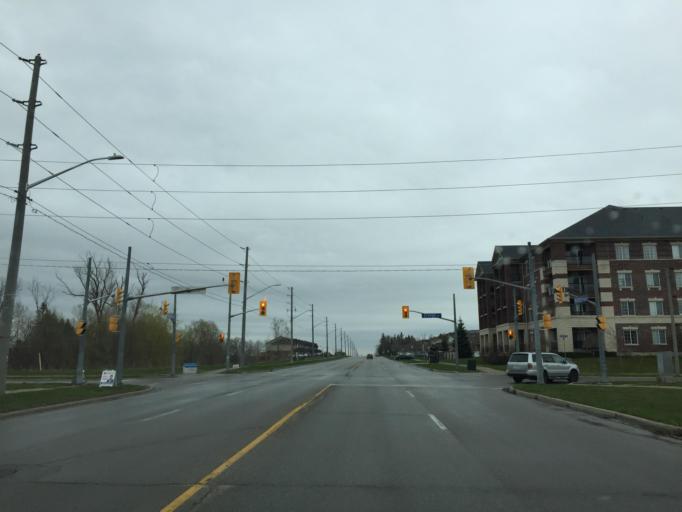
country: CA
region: Ontario
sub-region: Wellington County
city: Guelph
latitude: 43.5739
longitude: -80.2185
